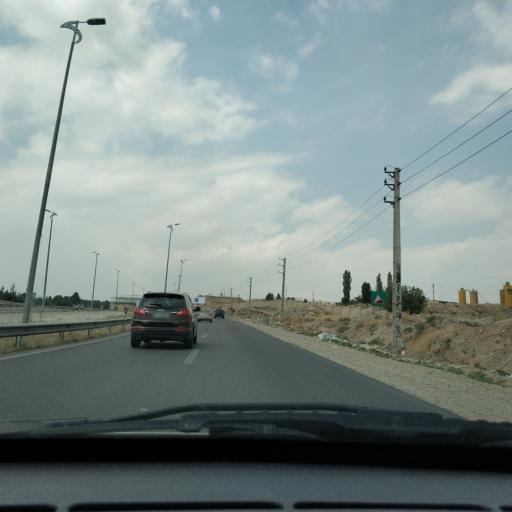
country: IR
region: Tehran
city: Tajrish
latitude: 35.7824
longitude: 51.5643
